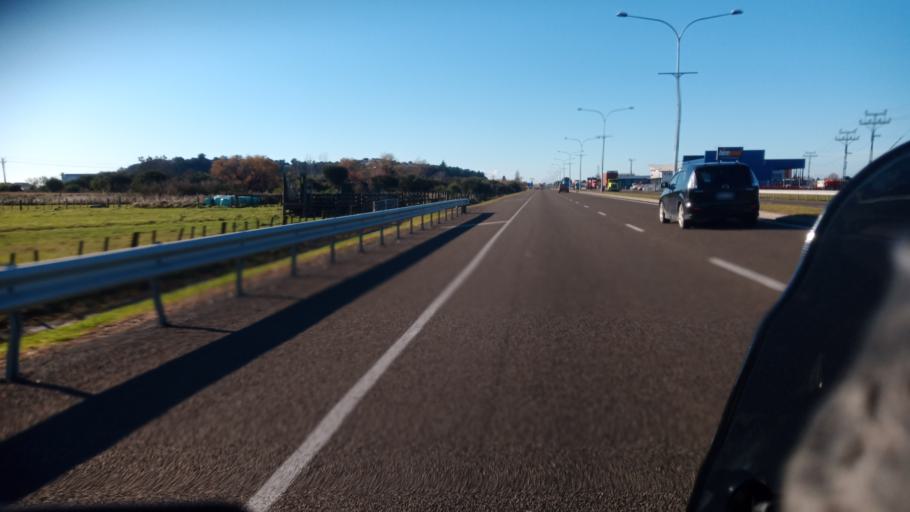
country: NZ
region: Hawke's Bay
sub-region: Napier City
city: Napier
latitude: -39.4963
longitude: 176.8788
